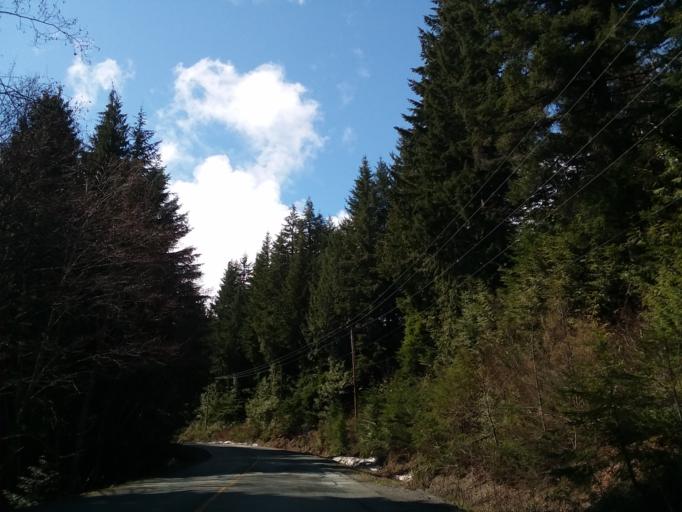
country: CA
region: British Columbia
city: Whistler
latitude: 50.1097
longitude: -122.9887
